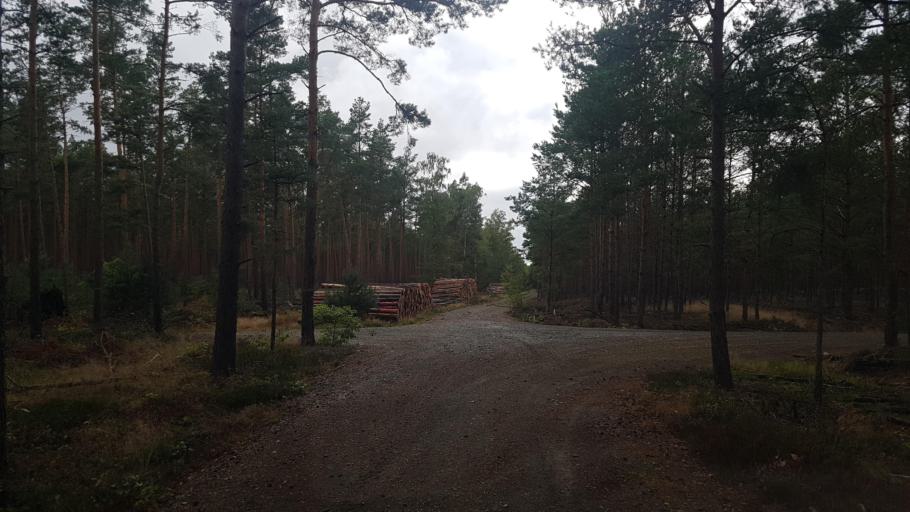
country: DE
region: Brandenburg
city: Elsterwerda
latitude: 51.4910
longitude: 13.4606
